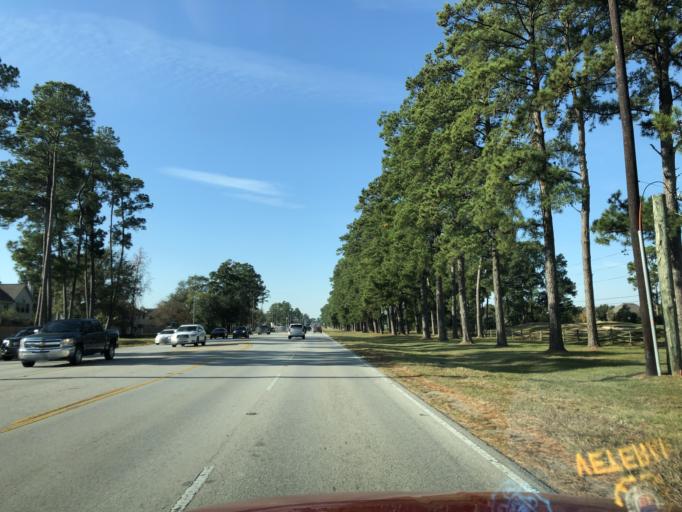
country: US
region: Texas
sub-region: Harris County
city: Tomball
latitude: 30.0293
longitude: -95.5593
